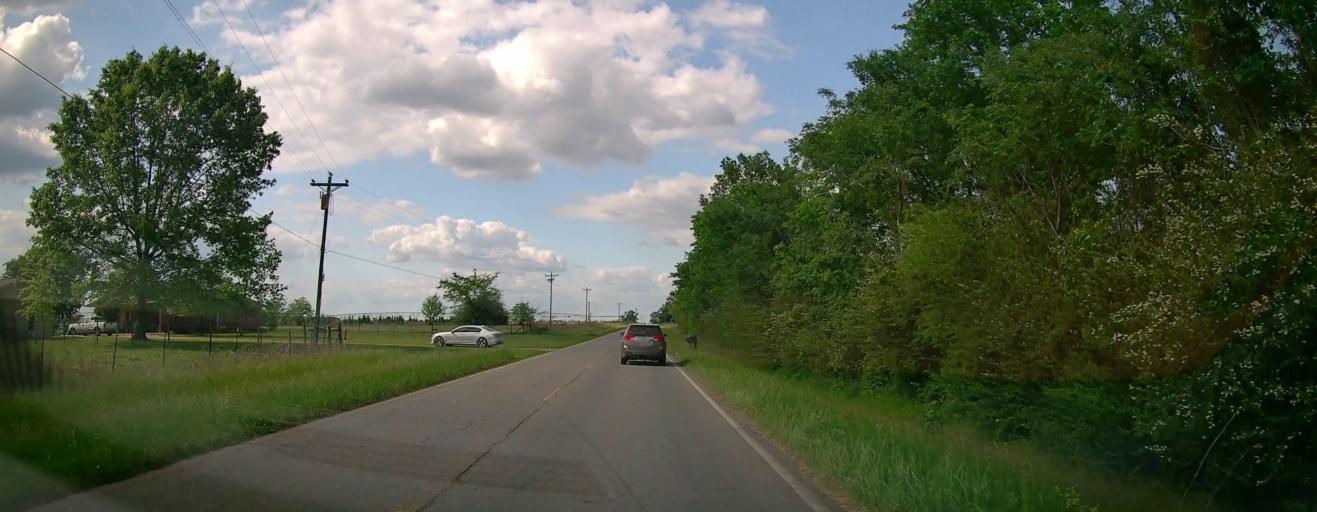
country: US
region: Georgia
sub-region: Laurens County
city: East Dublin
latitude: 32.6040
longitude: -82.8672
